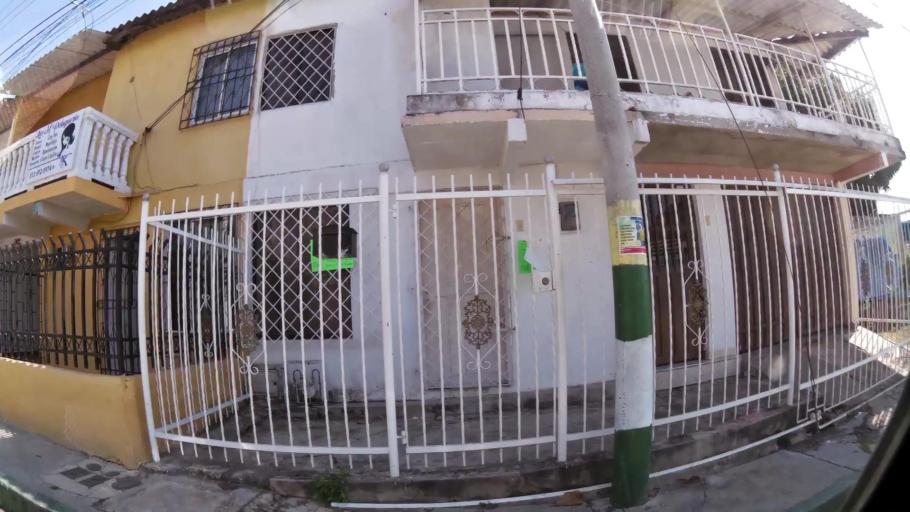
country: CO
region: Bolivar
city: Cartagena
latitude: 10.3945
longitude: -75.5059
